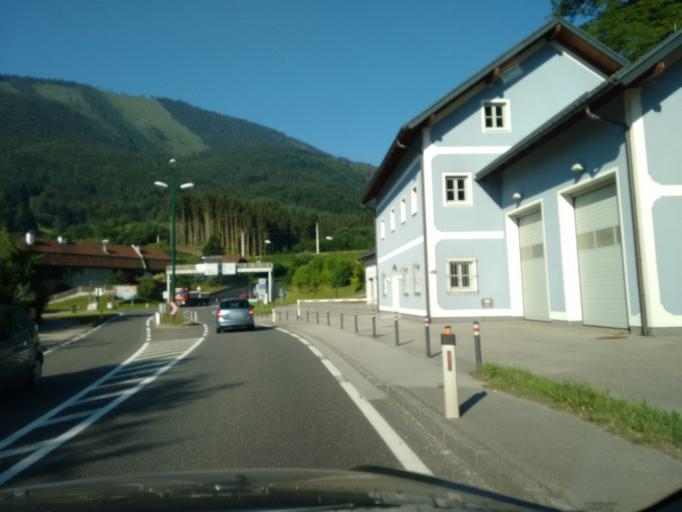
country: AT
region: Upper Austria
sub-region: Politischer Bezirk Gmunden
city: Ebensee
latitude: 47.8522
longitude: 13.7775
